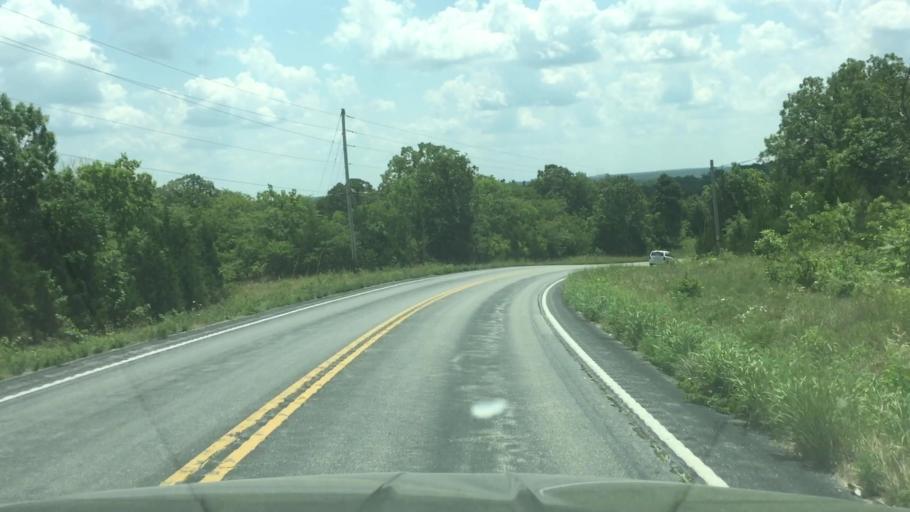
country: US
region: Missouri
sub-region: Miller County
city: Tuscumbia
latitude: 38.1053
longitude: -92.4996
